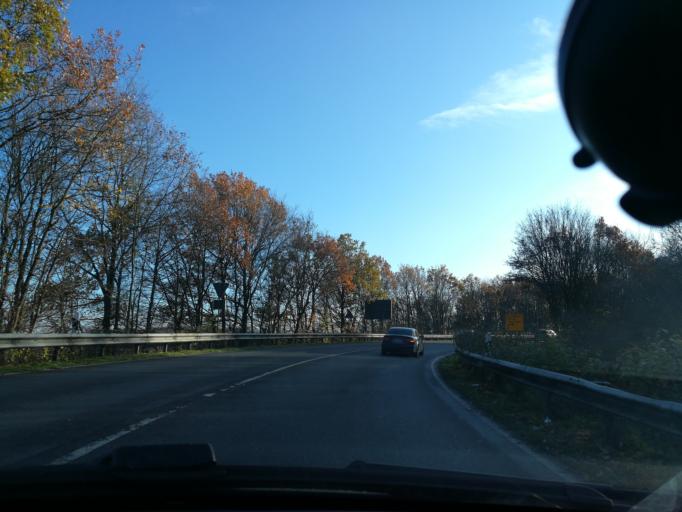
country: DE
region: North Rhine-Westphalia
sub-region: Regierungsbezirk Detmold
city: Petershagen
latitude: 52.3775
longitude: 8.9988
